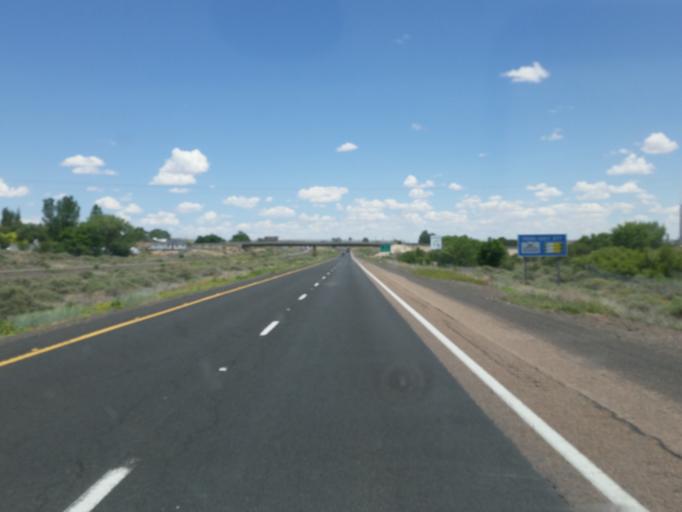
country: US
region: Arizona
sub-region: Navajo County
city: Joseph City
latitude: 34.9542
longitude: -110.3355
